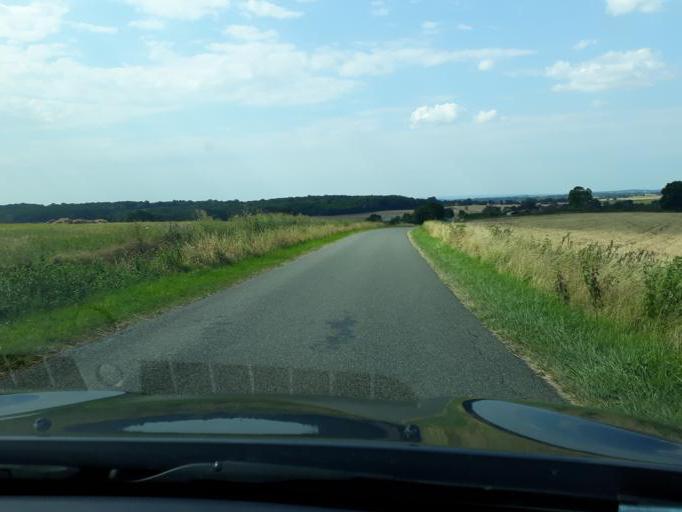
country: FR
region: Centre
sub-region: Departement du Cher
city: Nerondes
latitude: 47.0255
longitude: 2.9013
